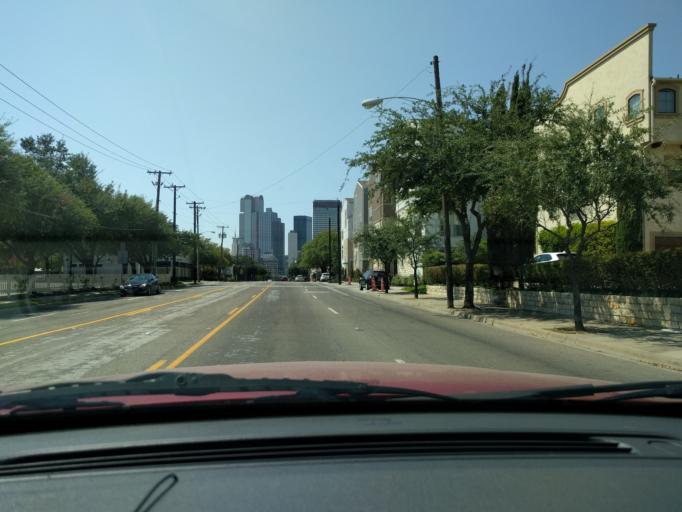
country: US
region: Texas
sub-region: Dallas County
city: Dallas
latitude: 32.7913
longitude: -96.7863
